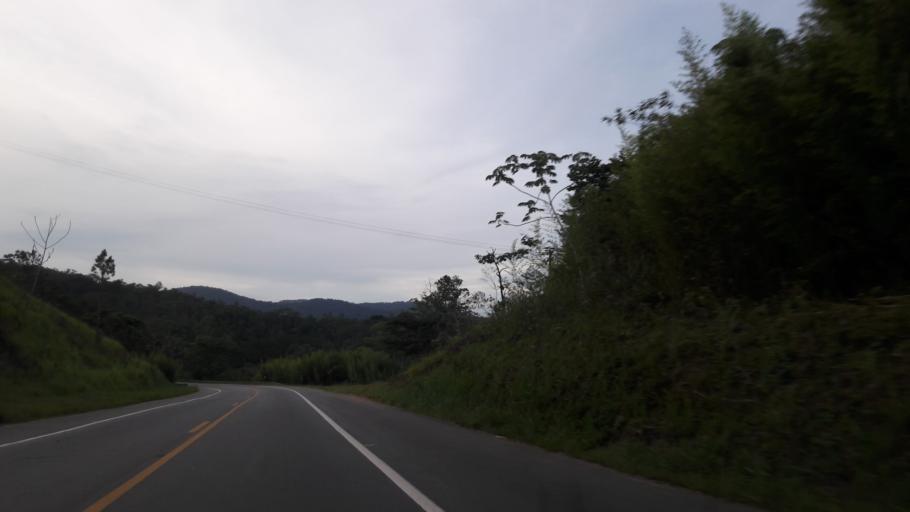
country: BR
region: Sao Paulo
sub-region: Miracatu
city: Miracatu
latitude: -24.2696
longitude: -47.2641
